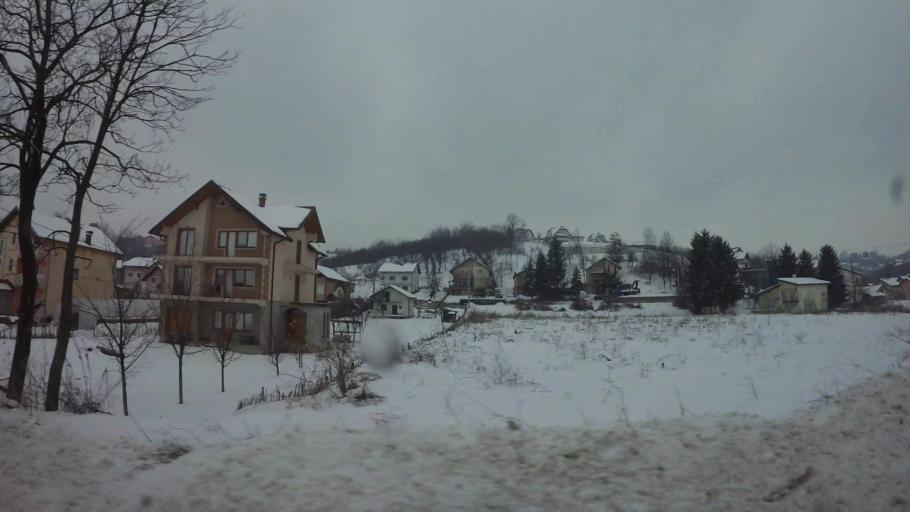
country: BA
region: Federation of Bosnia and Herzegovina
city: Hadzici
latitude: 43.8539
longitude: 18.2744
